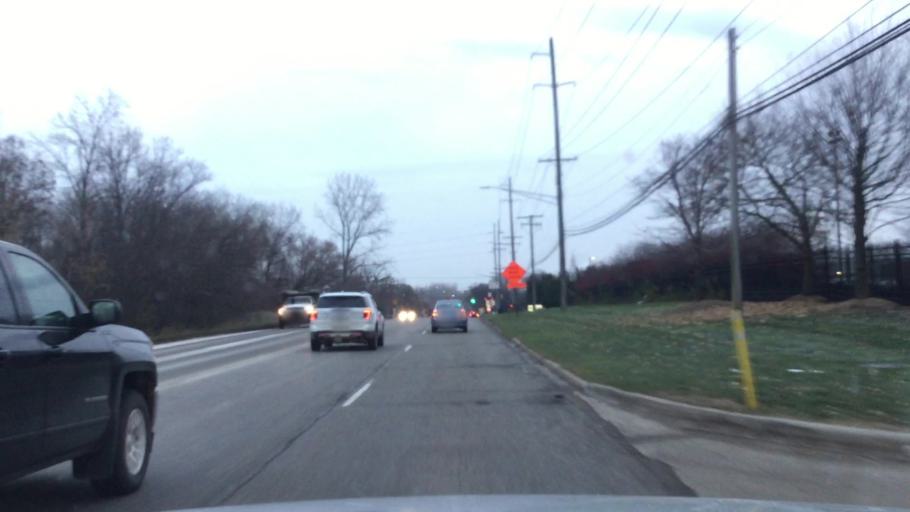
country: US
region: Michigan
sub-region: Oakland County
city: Pontiac
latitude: 42.6352
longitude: -83.2529
